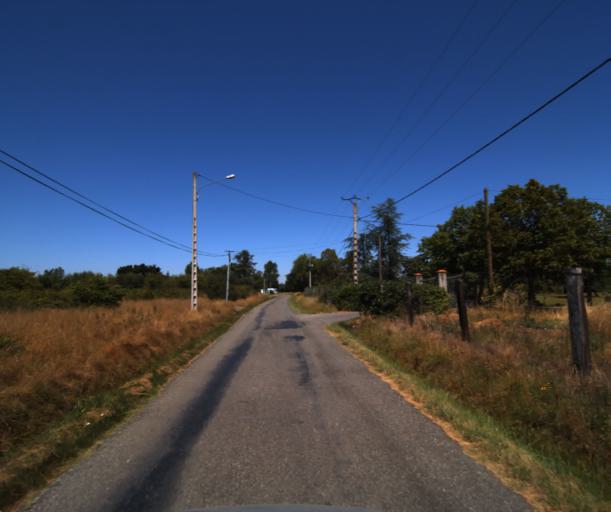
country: FR
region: Midi-Pyrenees
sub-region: Departement de la Haute-Garonne
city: Seysses
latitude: 43.4767
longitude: 1.2933
